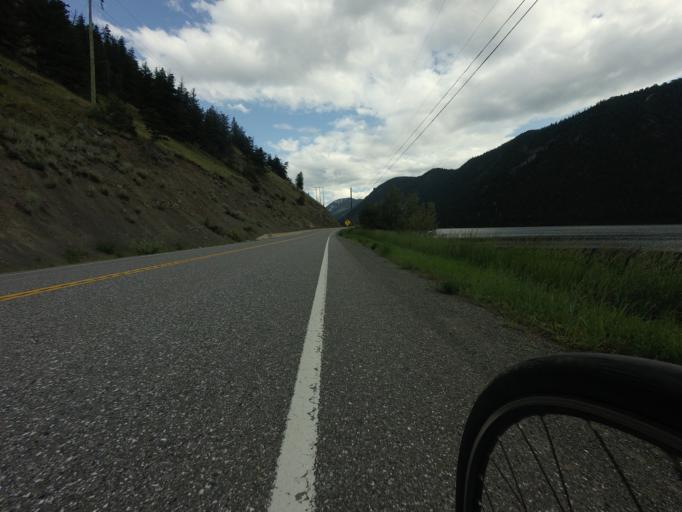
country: CA
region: British Columbia
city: Lillooet
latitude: 50.8689
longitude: -121.7372
